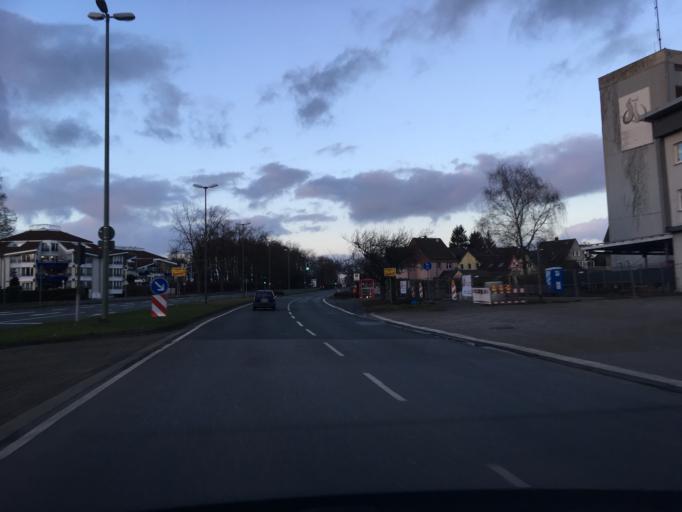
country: DE
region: North Rhine-Westphalia
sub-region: Regierungsbezirk Munster
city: Bottrop
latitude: 51.5317
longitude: 6.9233
